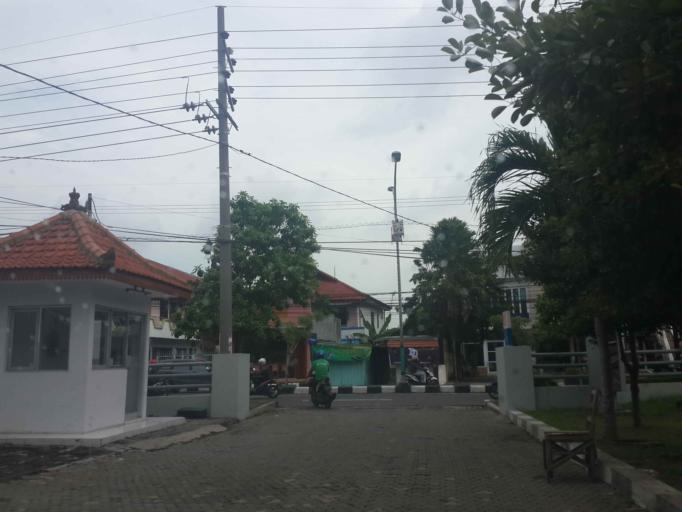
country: ID
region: East Java
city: Kebomas
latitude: -7.1670
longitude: 112.6413
